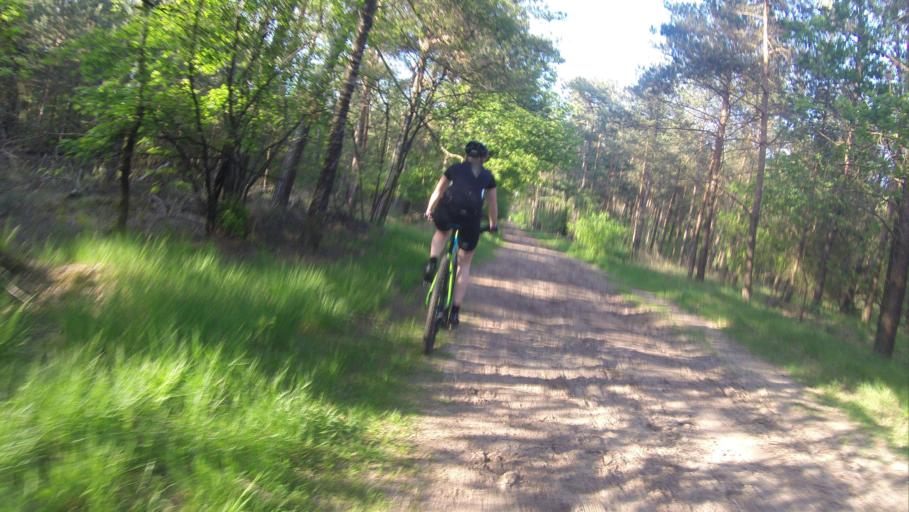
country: NL
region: Gelderland
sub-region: Gemeente Lochem
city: Almen
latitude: 52.1313
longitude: 6.3453
